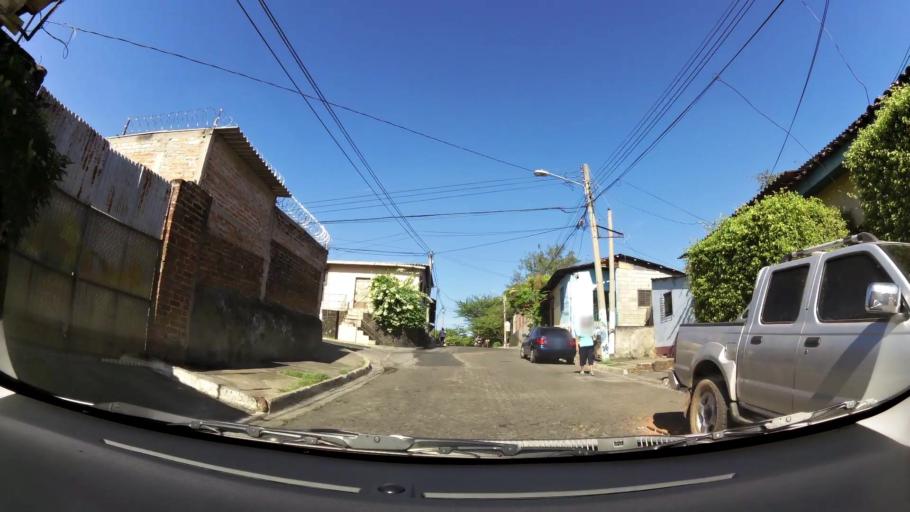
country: SV
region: Sonsonate
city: Sonsonate
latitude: 13.7251
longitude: -89.7249
